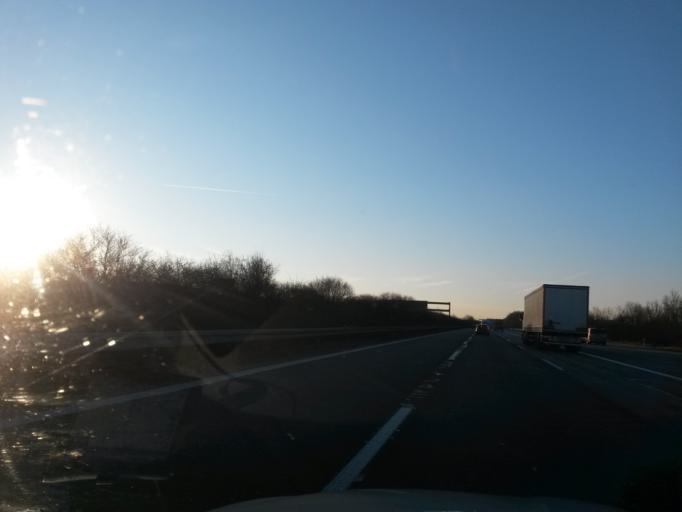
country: DE
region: Bavaria
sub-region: Upper Bavaria
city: Kirchheim bei Muenchen
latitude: 48.1663
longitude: 11.7414
